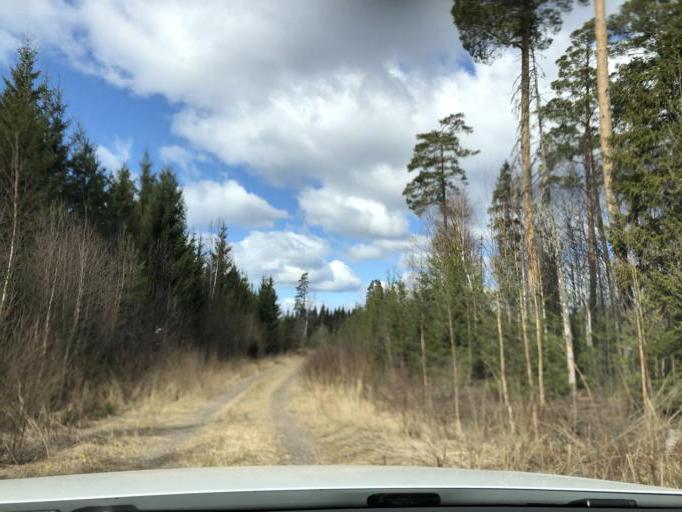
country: SE
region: Uppsala
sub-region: Tierps Kommun
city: Tierp
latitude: 60.3314
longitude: 17.3376
